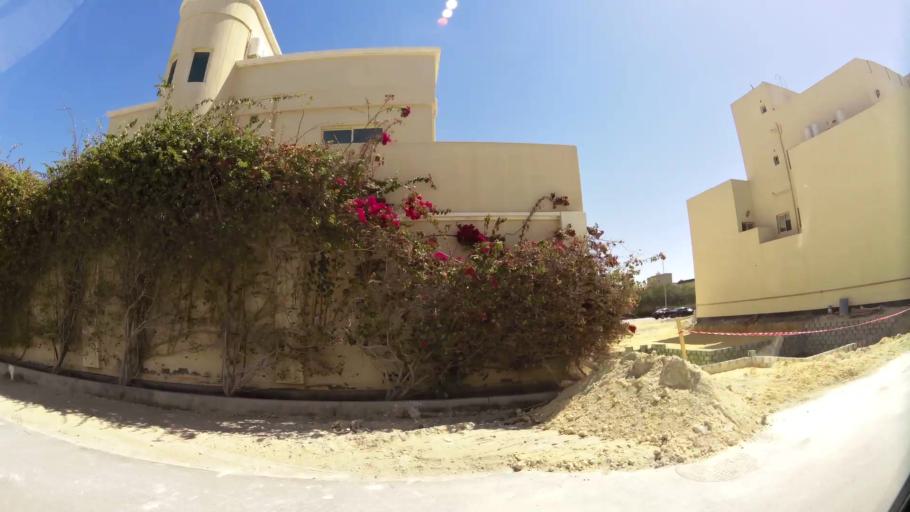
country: BH
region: Muharraq
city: Al Muharraq
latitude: 26.2760
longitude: 50.6023
